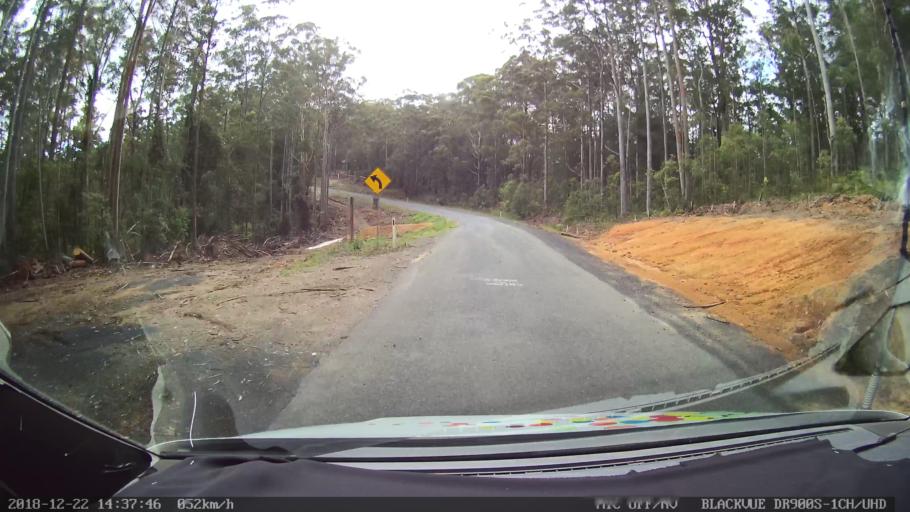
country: AU
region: New South Wales
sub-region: Bellingen
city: Dorrigo
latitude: -30.1343
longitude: 152.5999
